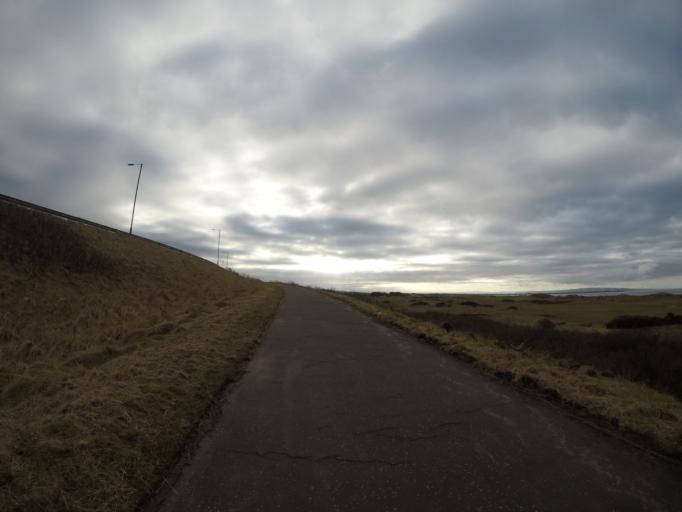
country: GB
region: Scotland
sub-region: North Ayrshire
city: Irvine
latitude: 55.5903
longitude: -4.6677
